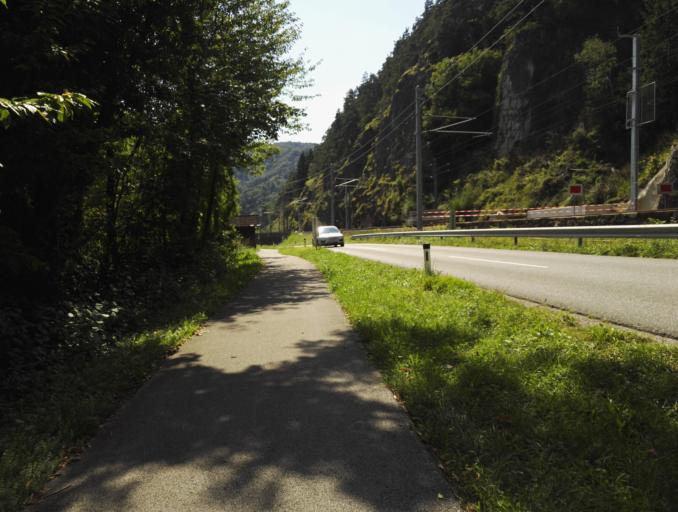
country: AT
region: Styria
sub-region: Politischer Bezirk Graz-Umgebung
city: Deutschfeistritz
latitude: 47.1645
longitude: 15.3179
